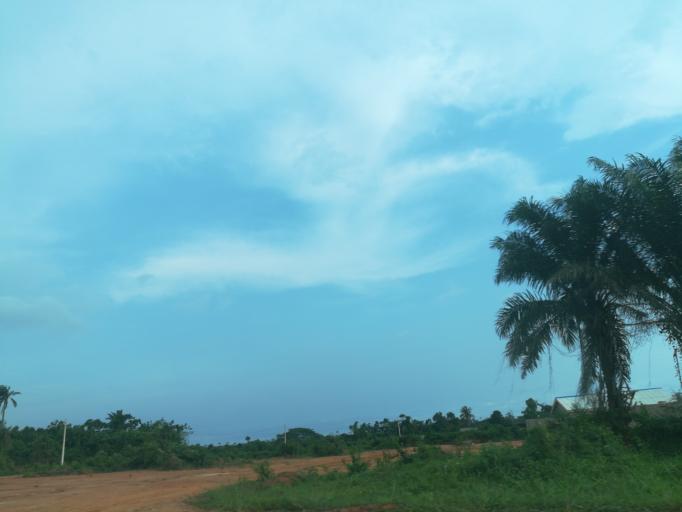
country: NG
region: Lagos
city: Ikorodu
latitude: 6.6333
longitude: 3.6686
